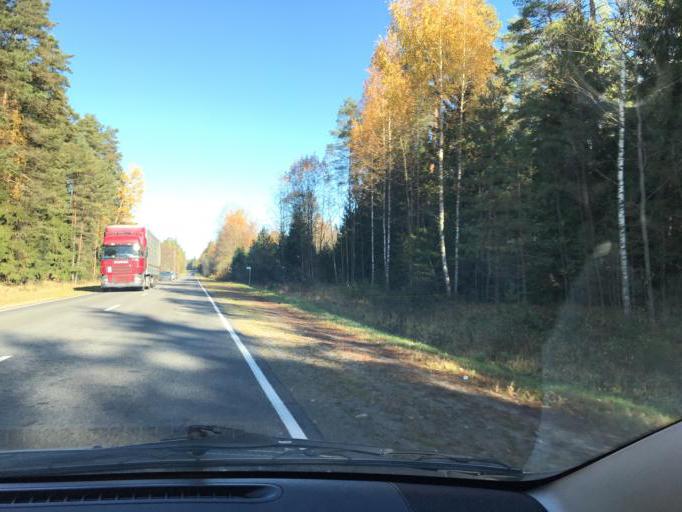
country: BY
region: Vitebsk
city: Lyepyel'
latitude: 54.9609
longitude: 28.7438
